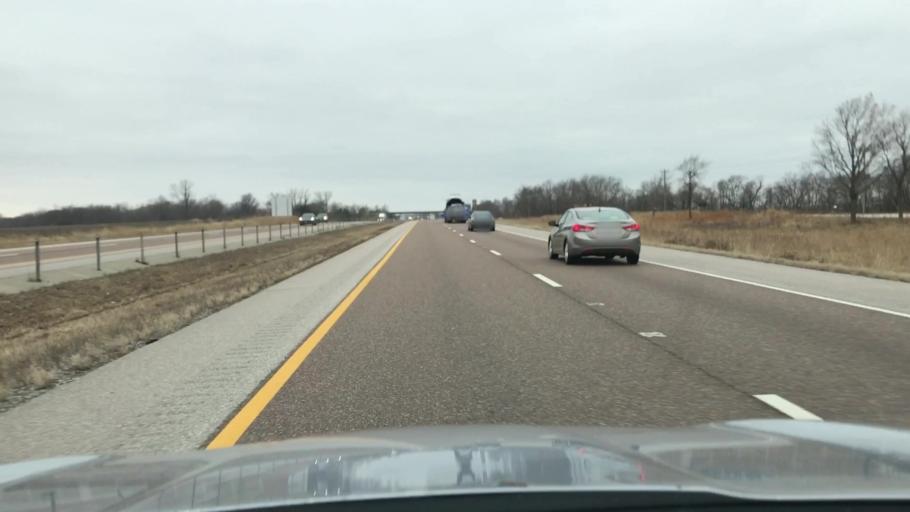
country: US
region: Illinois
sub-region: Madison County
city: Worden
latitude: 38.9160
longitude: -89.8172
